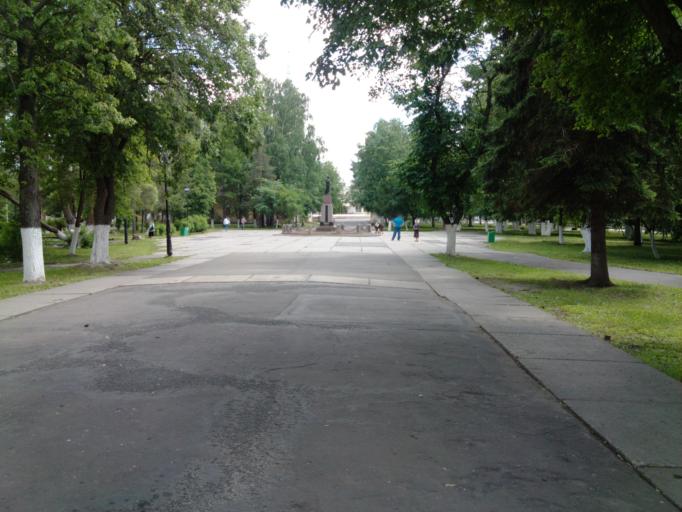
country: RU
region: Vologda
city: Vologda
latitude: 59.2187
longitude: 39.8941
